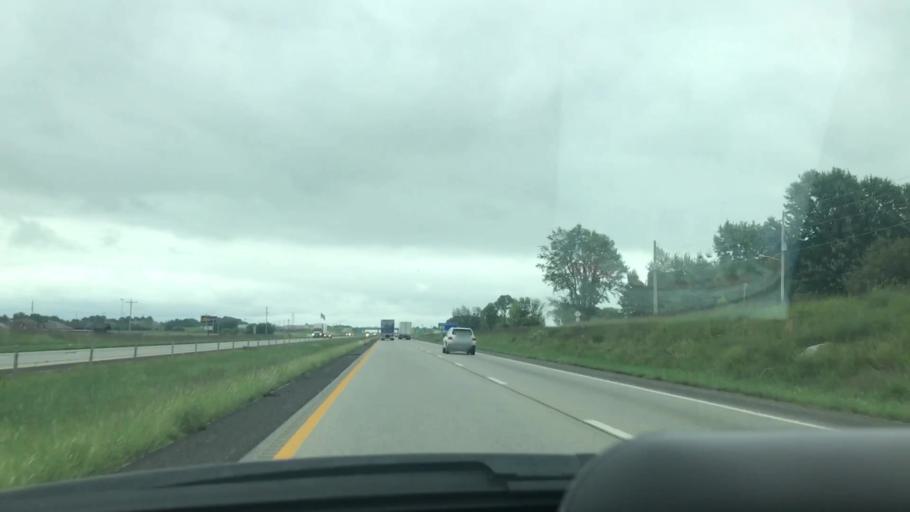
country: US
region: Missouri
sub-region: Greene County
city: Republic
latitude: 37.1986
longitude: -93.4320
